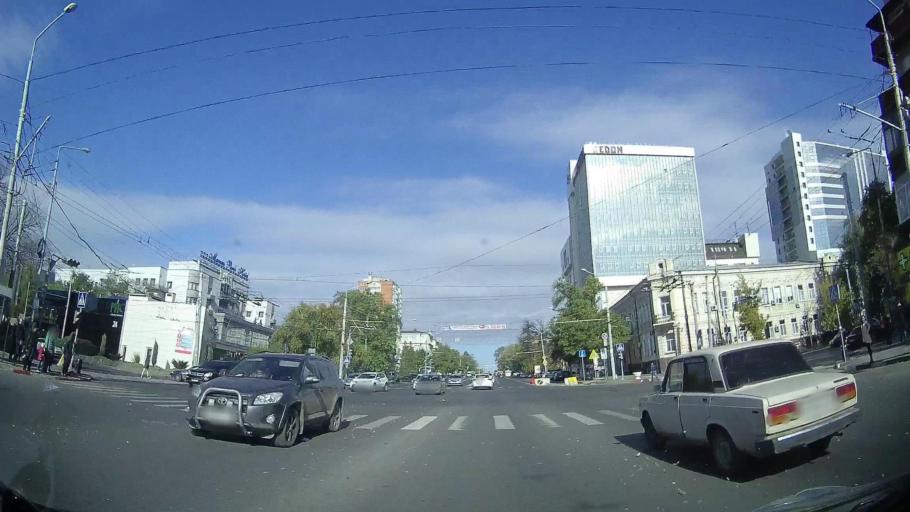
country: RU
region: Rostov
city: Rostov-na-Donu
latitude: 47.2260
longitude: 39.7050
